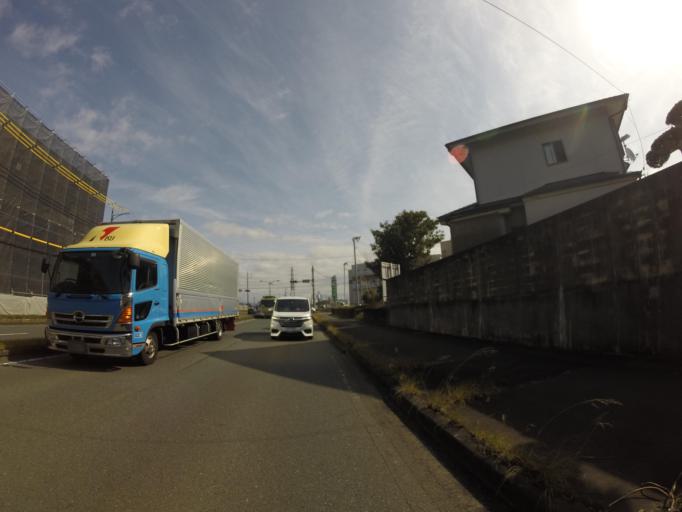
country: JP
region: Shizuoka
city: Hamamatsu
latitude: 34.7733
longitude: 137.6934
